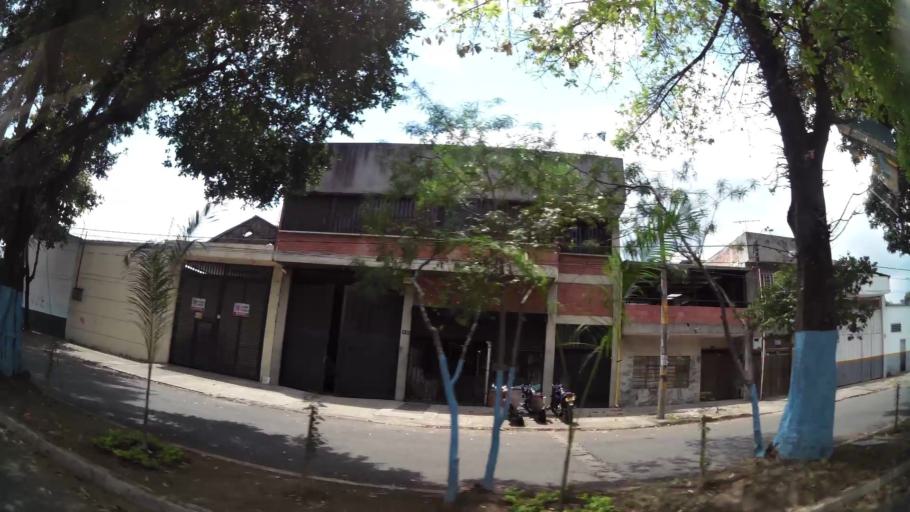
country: CO
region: Valle del Cauca
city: Cali
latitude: 3.4532
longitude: -76.5075
